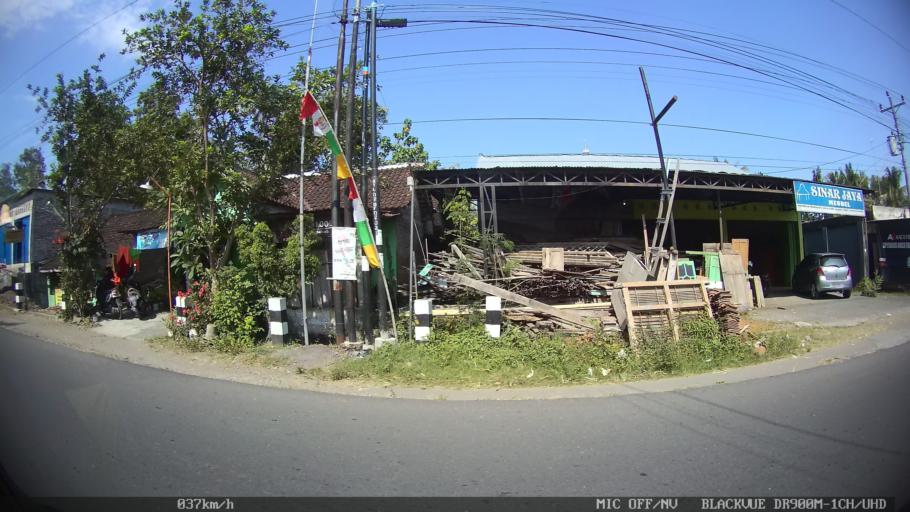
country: ID
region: Daerah Istimewa Yogyakarta
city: Sewon
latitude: -7.9058
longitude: 110.3838
